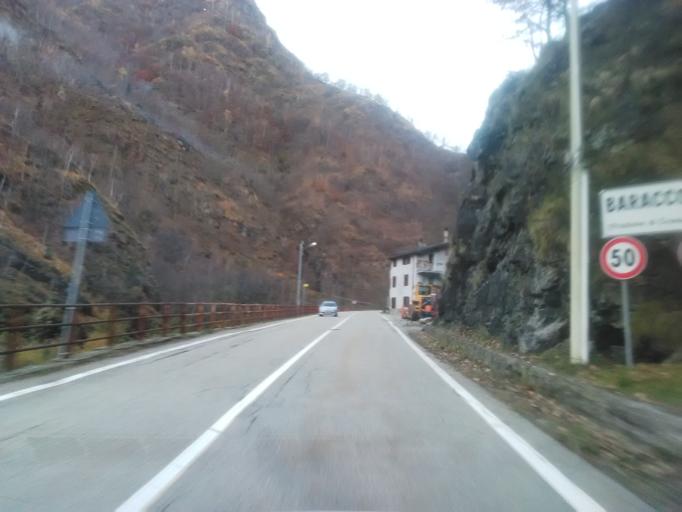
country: IT
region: Piedmont
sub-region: Provincia di Vercelli
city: Cervatto
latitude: 45.8770
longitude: 8.1773
